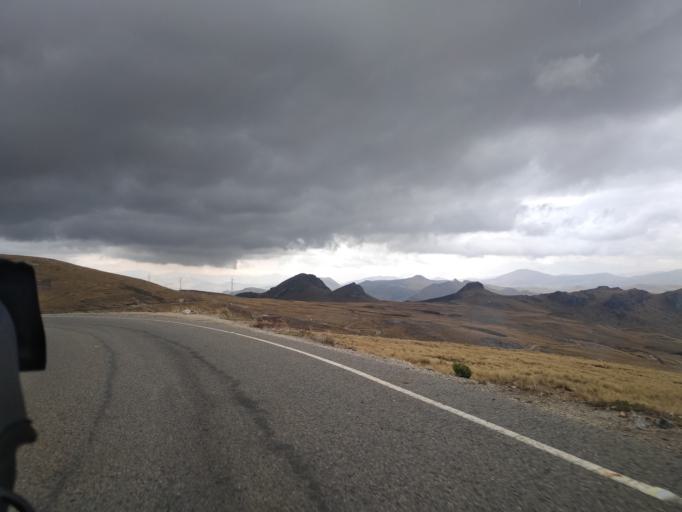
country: PE
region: La Libertad
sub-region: Provincia de Santiago de Chuco
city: Quiruvilca
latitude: -7.9929
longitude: -78.3066
